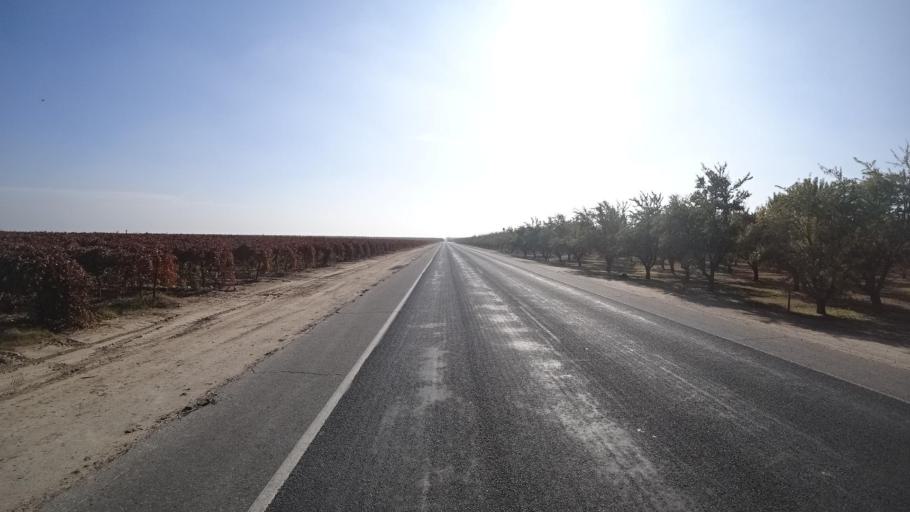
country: US
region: California
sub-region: Kern County
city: McFarland
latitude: 35.6507
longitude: -119.1956
